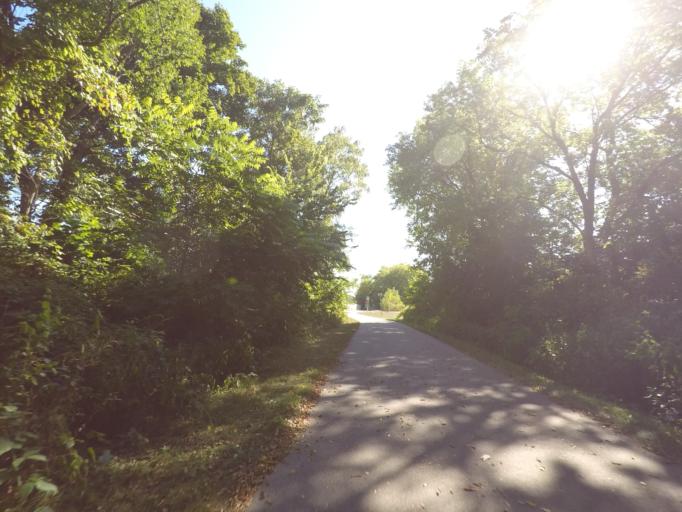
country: US
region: Wisconsin
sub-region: Waukesha County
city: Waukesha
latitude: 43.0085
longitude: -88.2131
